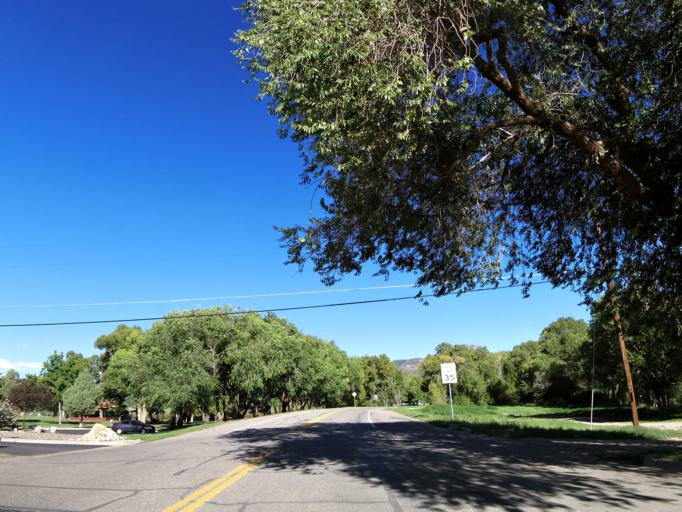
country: US
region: Colorado
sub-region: Montezuma County
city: Mancos
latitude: 37.3451
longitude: -108.2887
